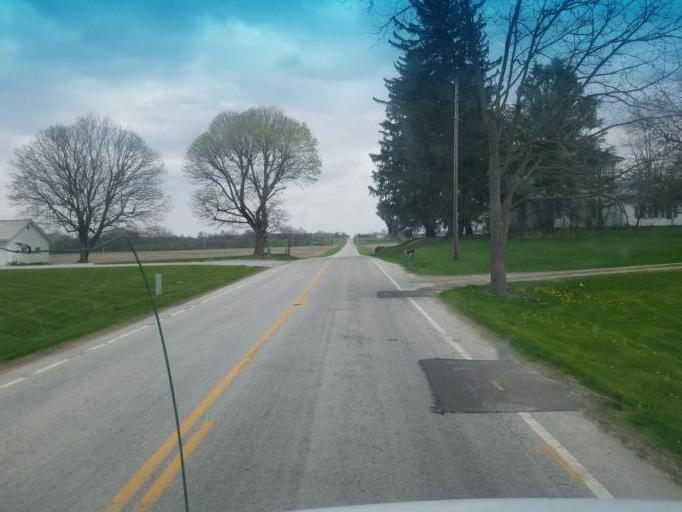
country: US
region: Ohio
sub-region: Seneca County
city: Tiffin
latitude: 40.9497
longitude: -83.1644
